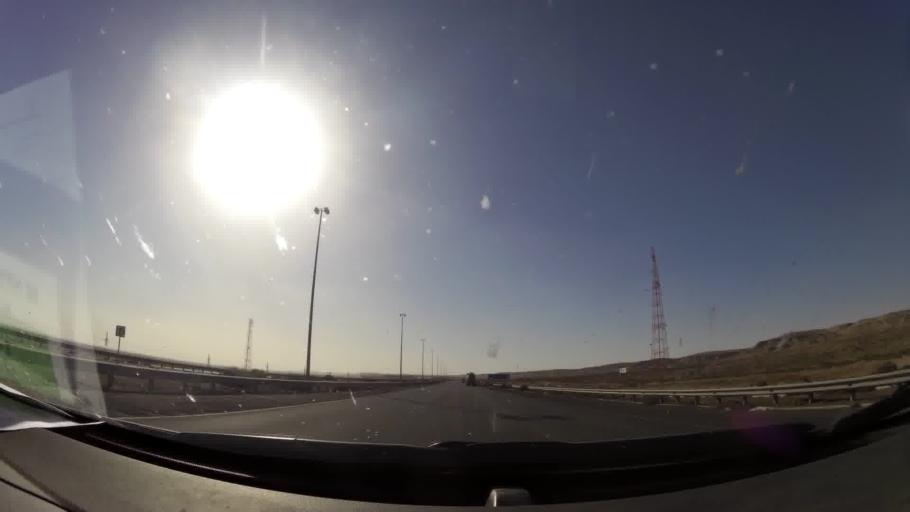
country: KW
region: Al Asimah
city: Kuwait City
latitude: 29.5350
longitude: 47.8371
